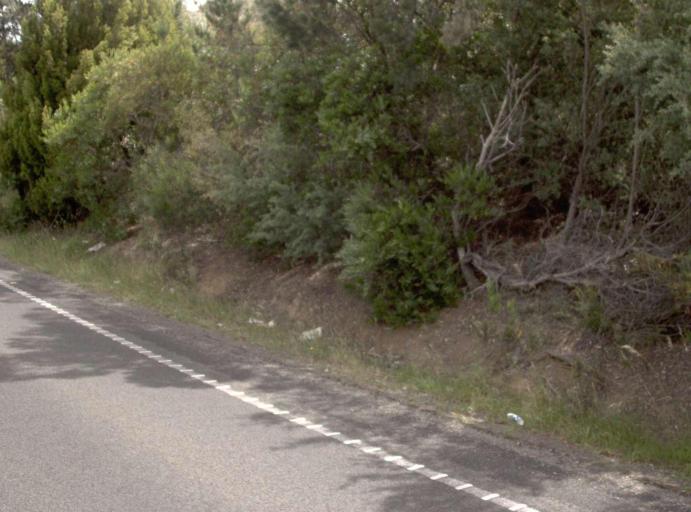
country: AU
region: Victoria
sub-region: Mornington Peninsula
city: Baxter
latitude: -38.1886
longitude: 145.1411
